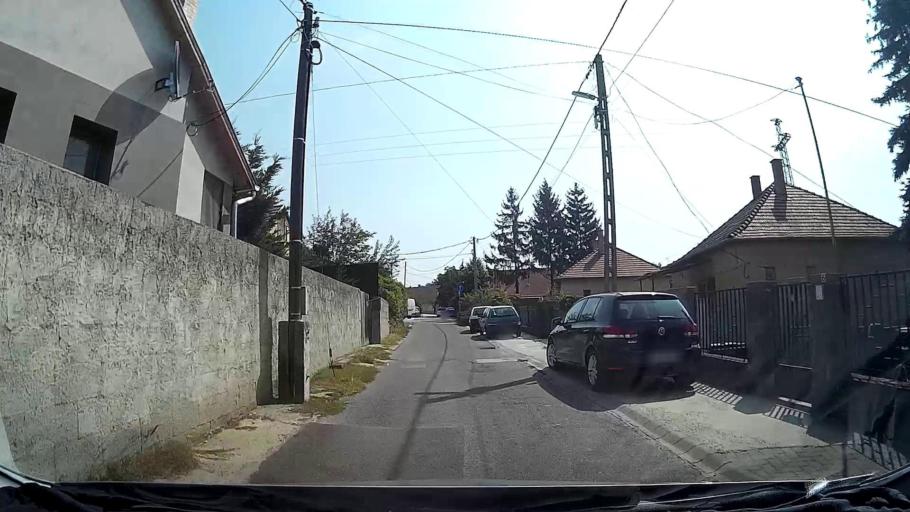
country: HU
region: Pest
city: Szentendre
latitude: 47.6792
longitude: 19.0562
